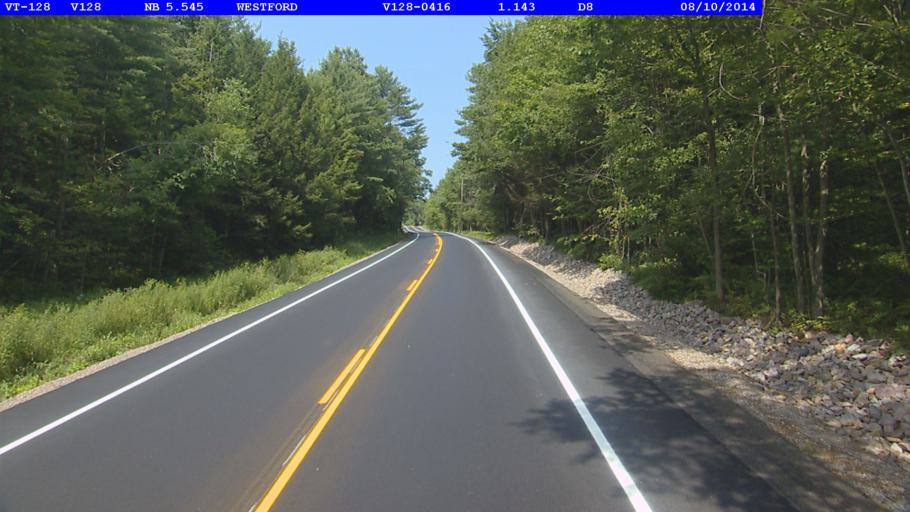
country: US
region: Vermont
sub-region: Chittenden County
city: Jericho
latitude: 44.5747
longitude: -73.0203
